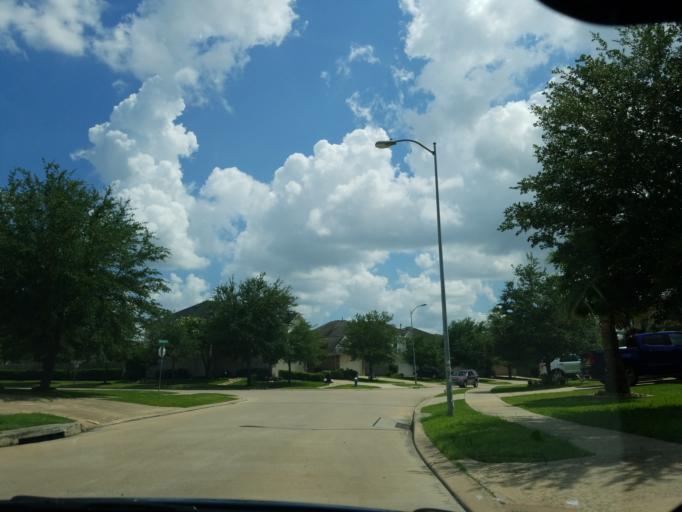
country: US
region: Texas
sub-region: Harris County
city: Cypress
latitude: 29.8755
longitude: -95.7260
